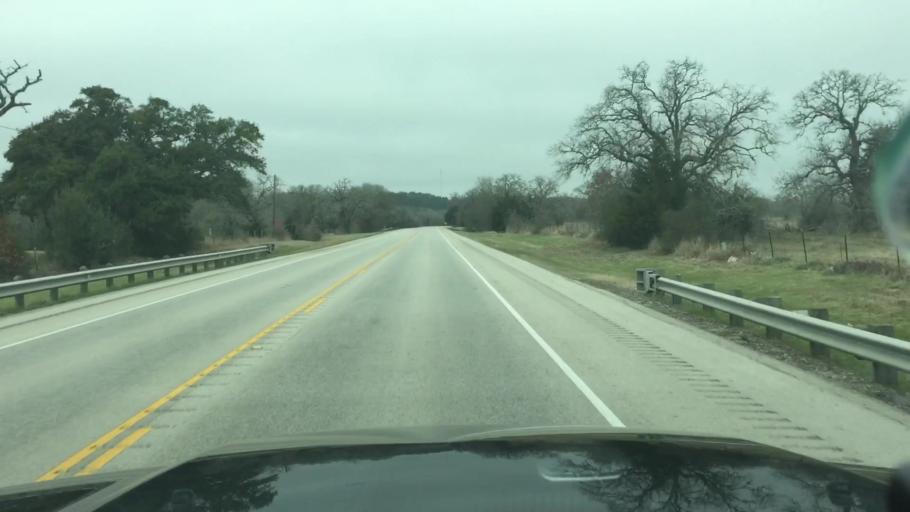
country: US
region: Texas
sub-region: Fayette County
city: La Grange
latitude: 30.0285
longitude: -96.9053
